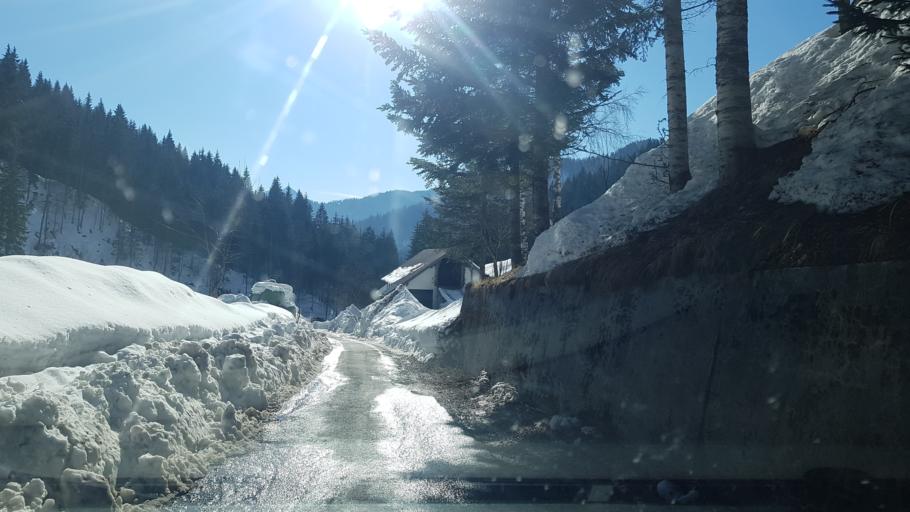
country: IT
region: Friuli Venezia Giulia
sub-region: Provincia di Udine
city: Malborghetto
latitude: 46.5484
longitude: 13.4790
